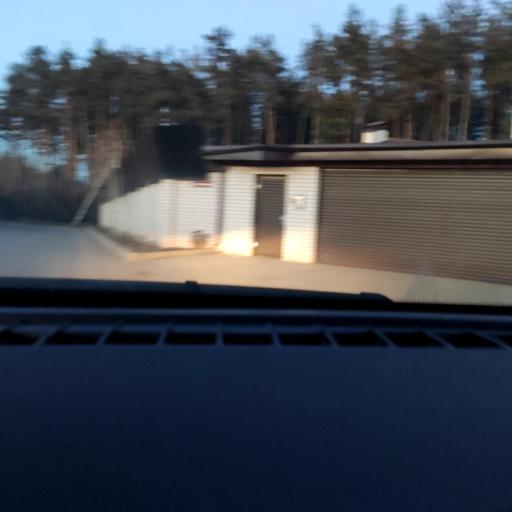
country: RU
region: Voronezj
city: Podgornoye
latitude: 51.7456
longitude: 39.1614
